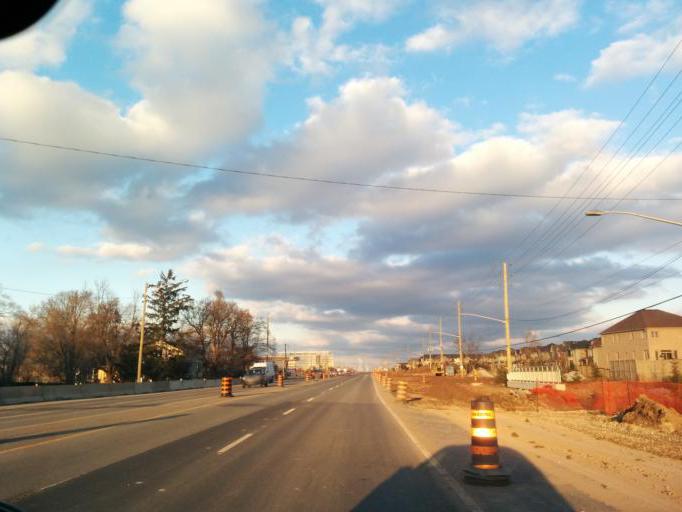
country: CA
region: Ontario
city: Burlington
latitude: 43.4385
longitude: -79.7734
